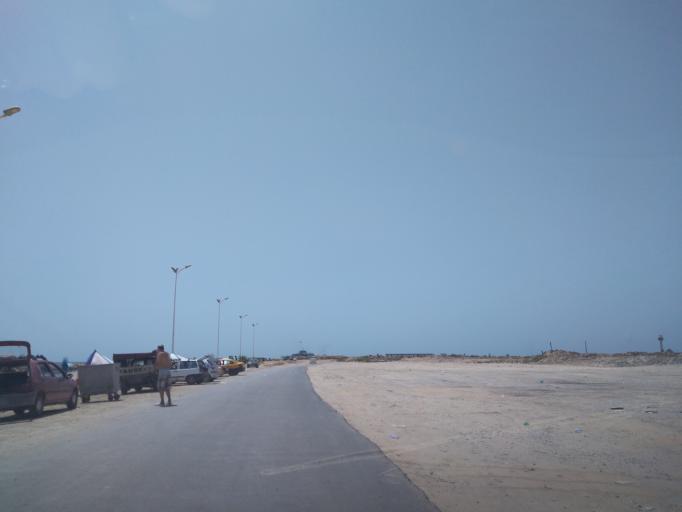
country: TN
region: Safaqis
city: Al Qarmadah
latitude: 34.7270
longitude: 10.7817
